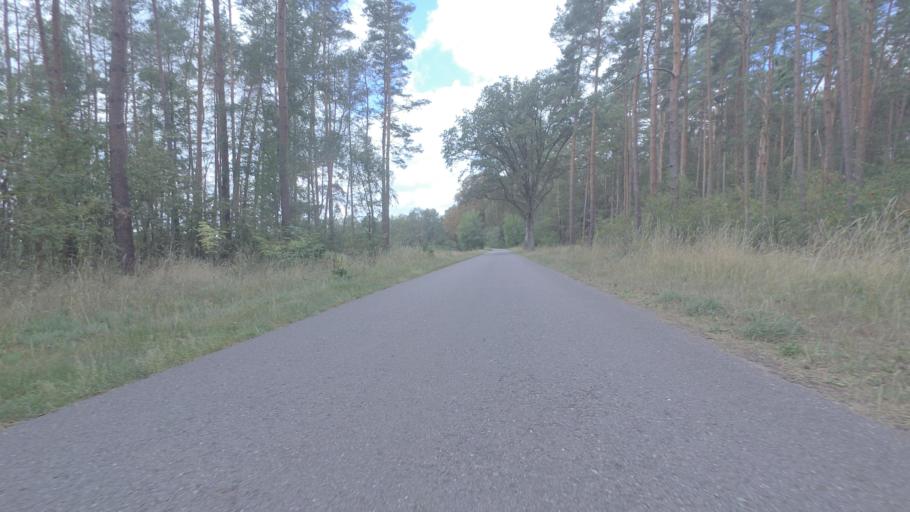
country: DE
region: Brandenburg
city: Wittstock
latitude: 53.0782
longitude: 12.4899
